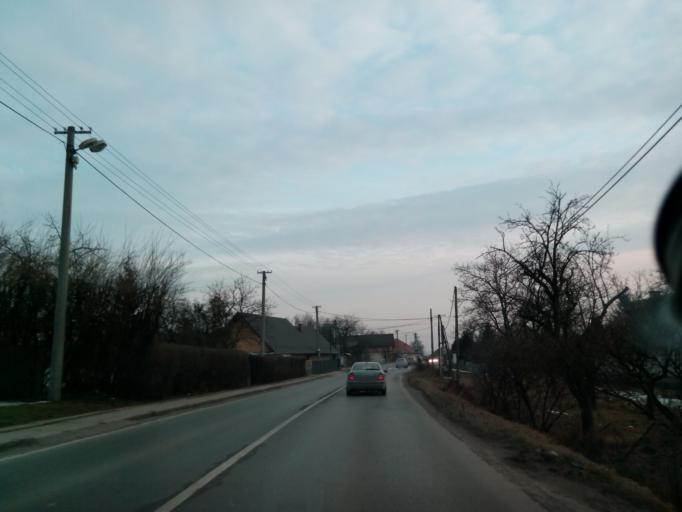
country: SK
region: Presovsky
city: Sabinov
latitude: 49.0904
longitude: 21.1138
